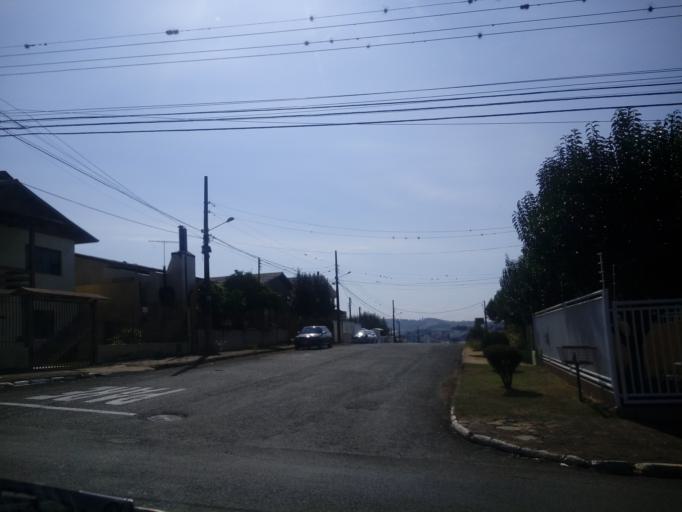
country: BR
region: Santa Catarina
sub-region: Chapeco
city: Chapeco
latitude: -27.0843
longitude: -52.6278
